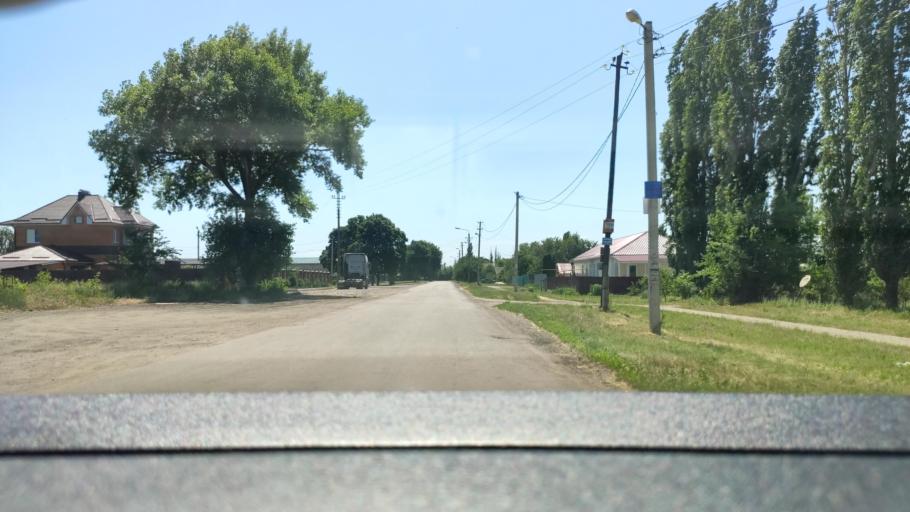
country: RU
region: Voronezj
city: Maslovka
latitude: 51.5090
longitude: 39.2940
